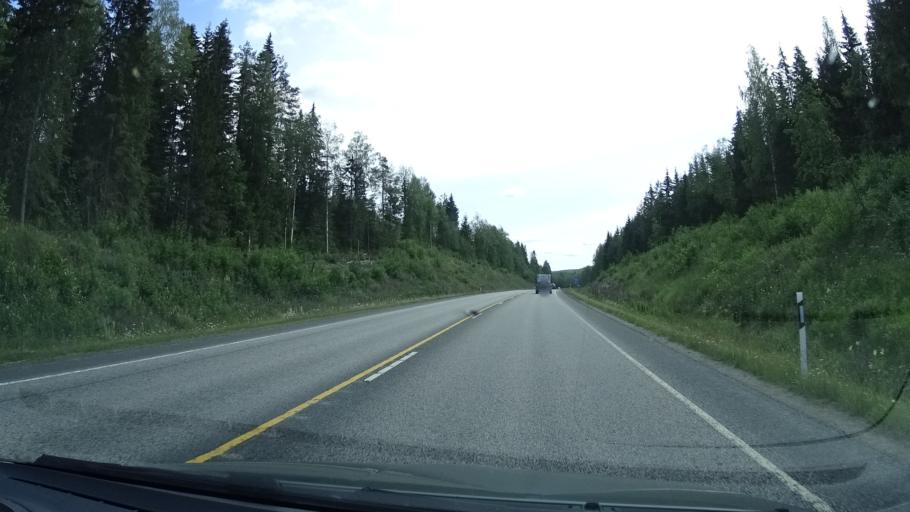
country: FI
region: Central Finland
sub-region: Jyvaeskylae
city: Jyvaeskylae
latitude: 62.2642
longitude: 25.5845
